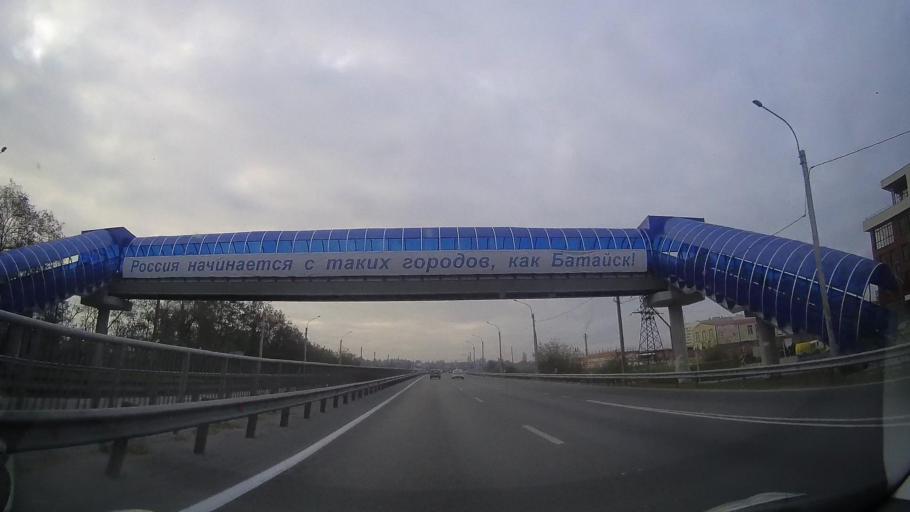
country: RU
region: Rostov
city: Bataysk
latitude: 47.1392
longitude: 39.7762
